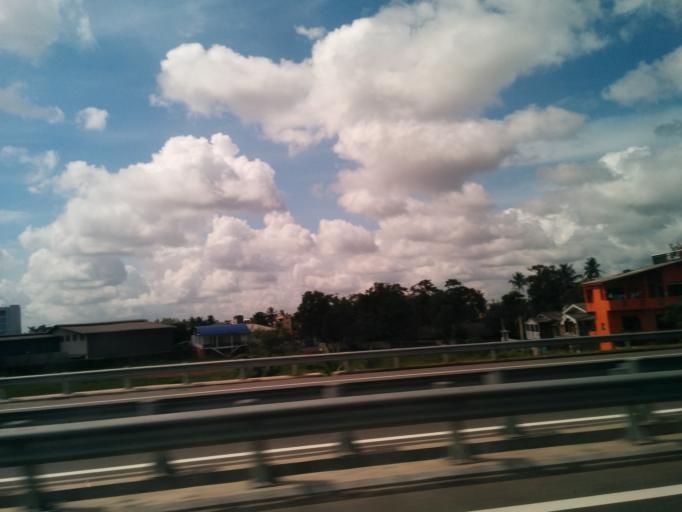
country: LK
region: Western
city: Peliyagoda
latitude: 6.9592
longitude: 79.8860
